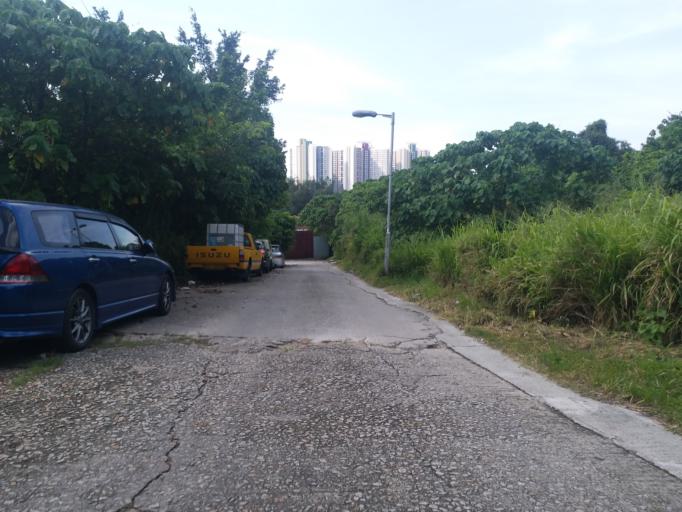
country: HK
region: Yuen Long
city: Yuen Long Kau Hui
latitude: 22.4386
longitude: 114.0011
